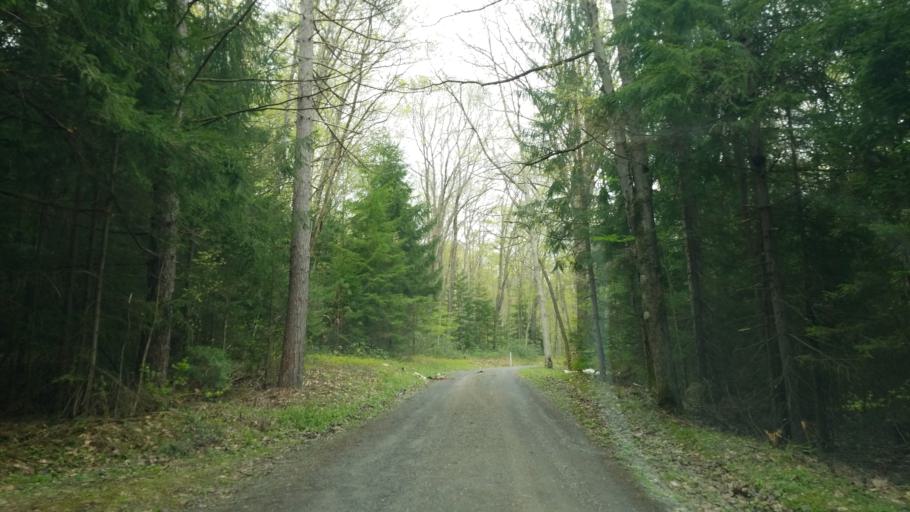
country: US
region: Pennsylvania
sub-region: Clearfield County
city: Shiloh
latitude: 41.2066
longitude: -78.1507
